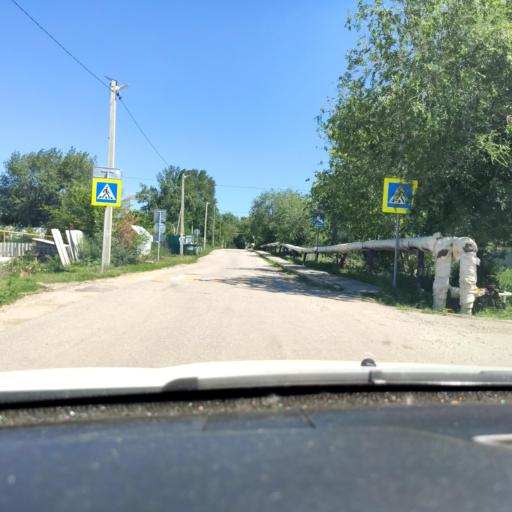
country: RU
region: Samara
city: Dubovyy Umet
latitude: 53.0358
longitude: 50.2442
